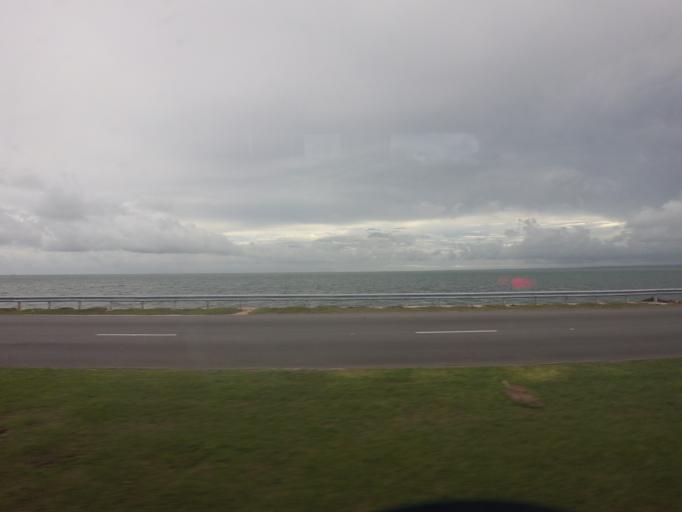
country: CU
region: Matanzas
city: Varadero
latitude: 23.1672
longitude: -81.2178
